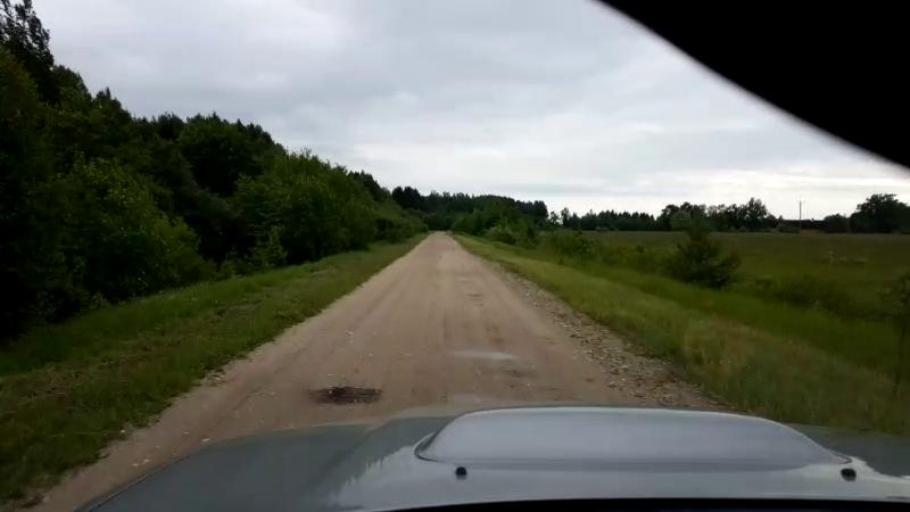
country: EE
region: Paernumaa
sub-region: Halinga vald
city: Parnu-Jaagupi
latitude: 58.5505
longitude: 24.5771
